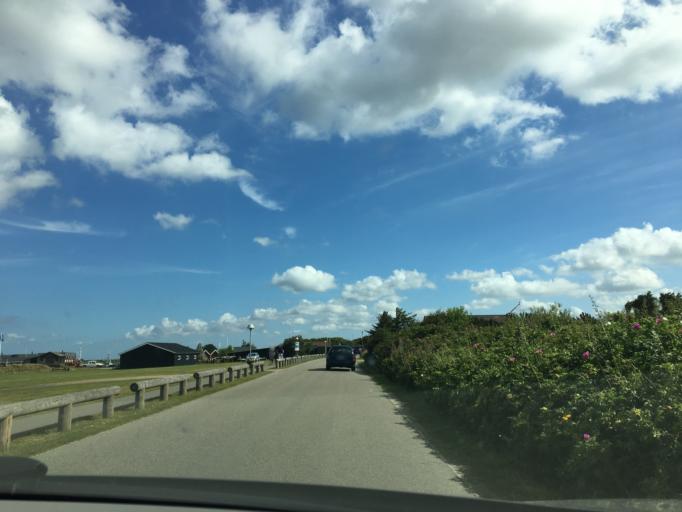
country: DK
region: Central Jutland
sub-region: Ringkobing-Skjern Kommune
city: Hvide Sande
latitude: 55.8476
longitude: 8.2787
